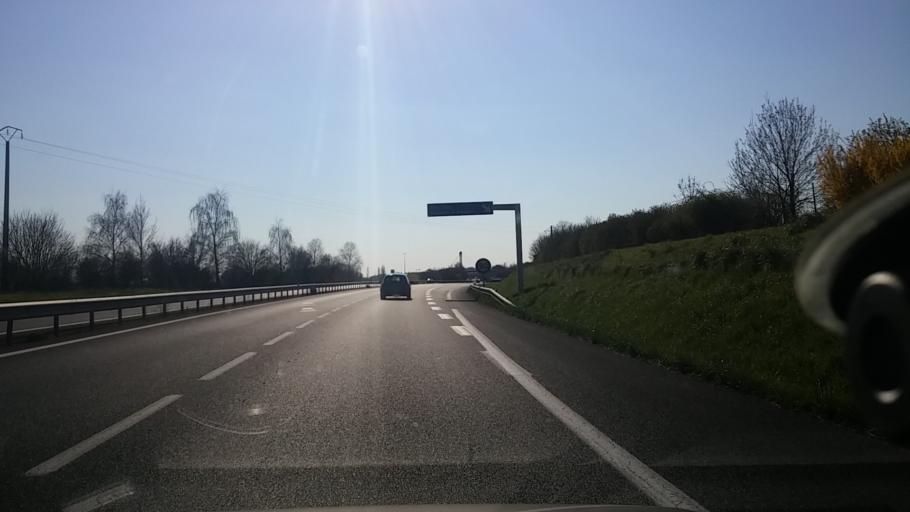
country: FR
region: Centre
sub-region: Departement de l'Indre
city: Vatan
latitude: 47.0907
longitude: 1.8526
